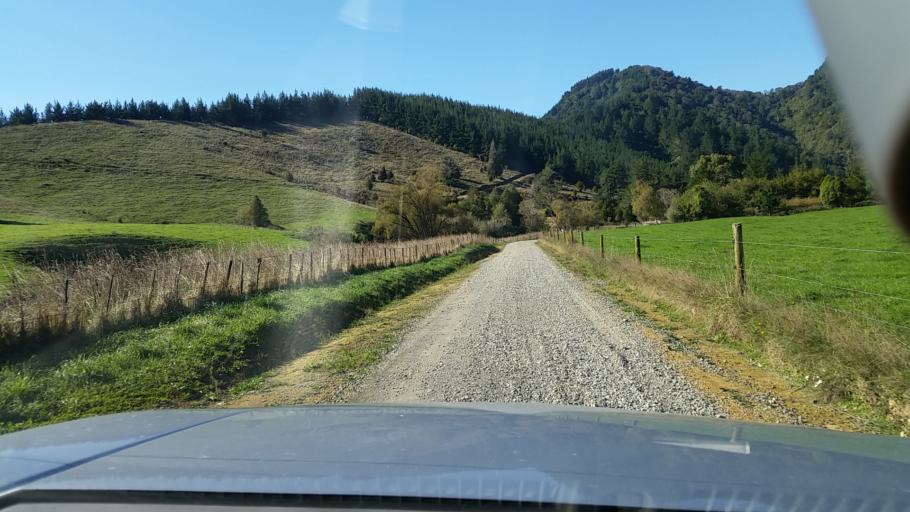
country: NZ
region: Nelson
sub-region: Nelson City
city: Nelson
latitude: -41.2216
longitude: 173.6096
